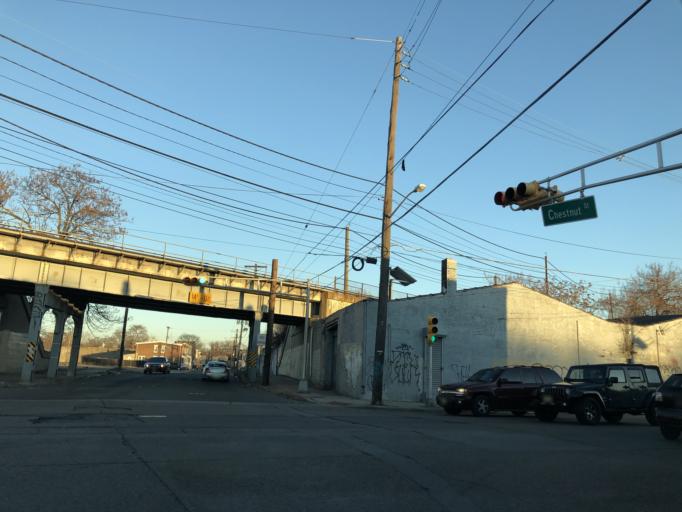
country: US
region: New Jersey
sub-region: Camden County
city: Camden
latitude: 39.9330
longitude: -75.1095
